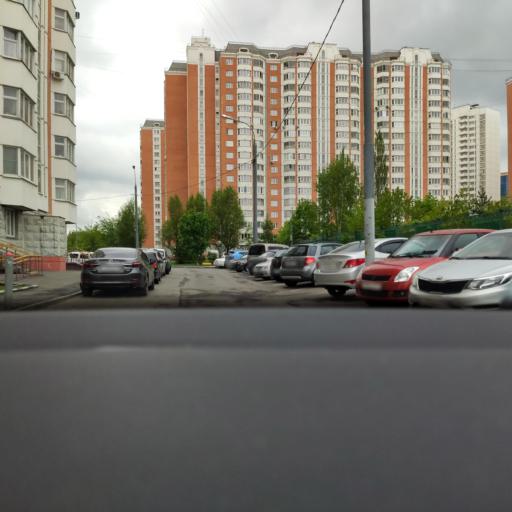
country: RU
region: Moscow
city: Vagonoremont
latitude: 55.9138
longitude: 37.5521
